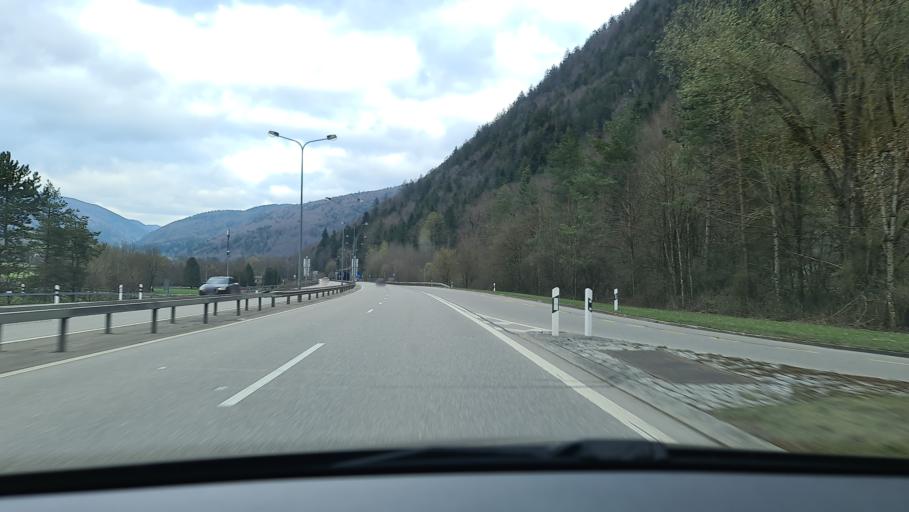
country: CH
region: Bern
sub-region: Jura bernois
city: Pery
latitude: 47.1871
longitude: 7.2294
